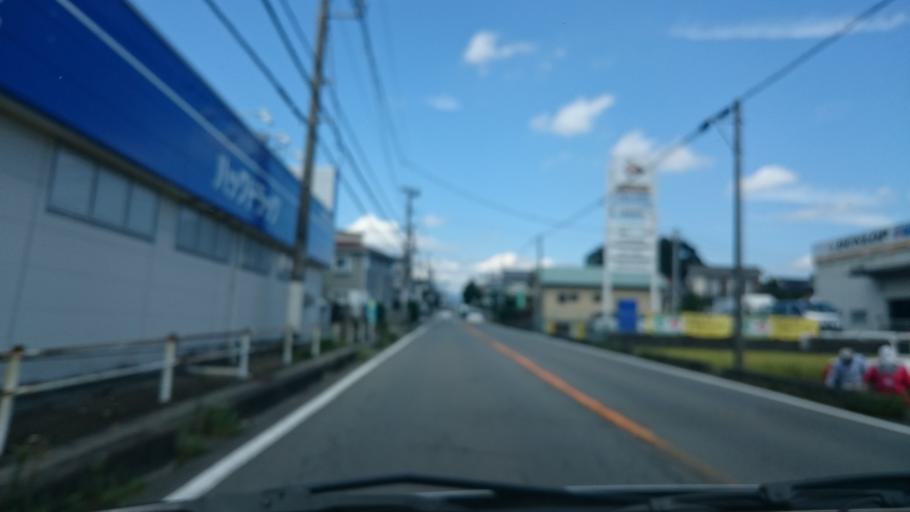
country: JP
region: Shizuoka
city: Gotemba
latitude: 35.2507
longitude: 138.9218
